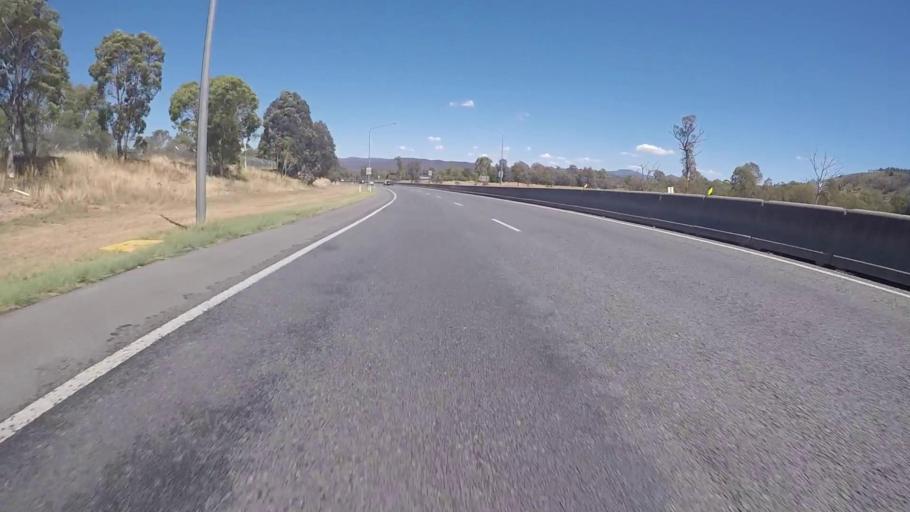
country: AU
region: Australian Capital Territory
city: Macarthur
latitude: -35.3701
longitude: 149.0585
